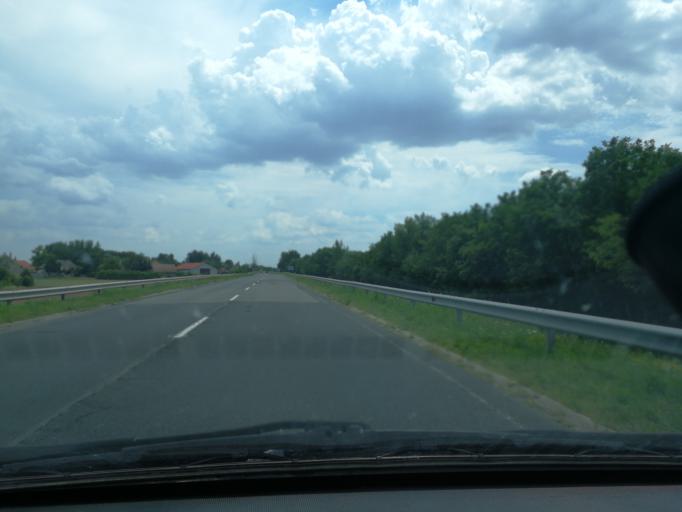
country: HU
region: Bacs-Kiskun
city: Harta
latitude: 46.7022
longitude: 19.0197
